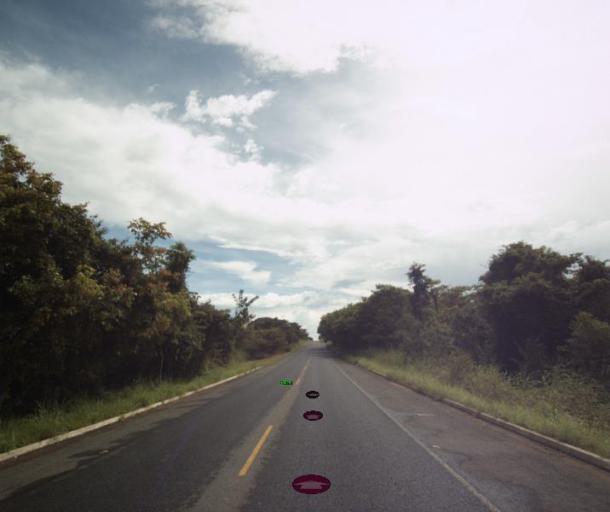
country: BR
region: Goias
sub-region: Sao Miguel Do Araguaia
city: Sao Miguel do Araguaia
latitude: -13.2874
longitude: -50.1964
